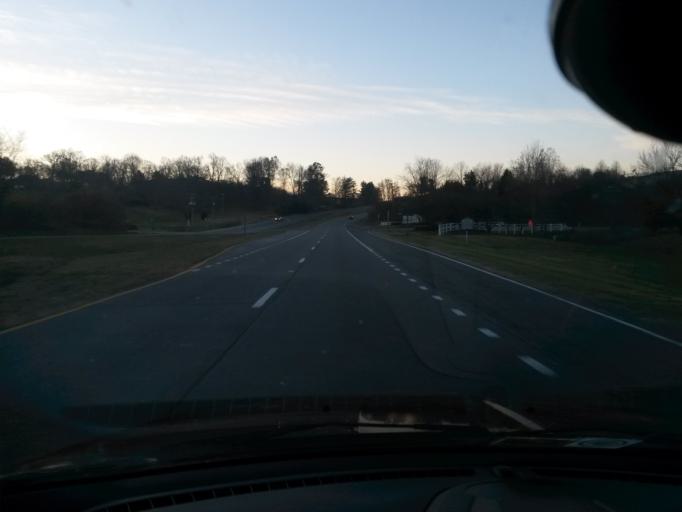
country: US
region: Virginia
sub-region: Botetourt County
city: Daleville
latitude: 37.4387
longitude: -79.9039
